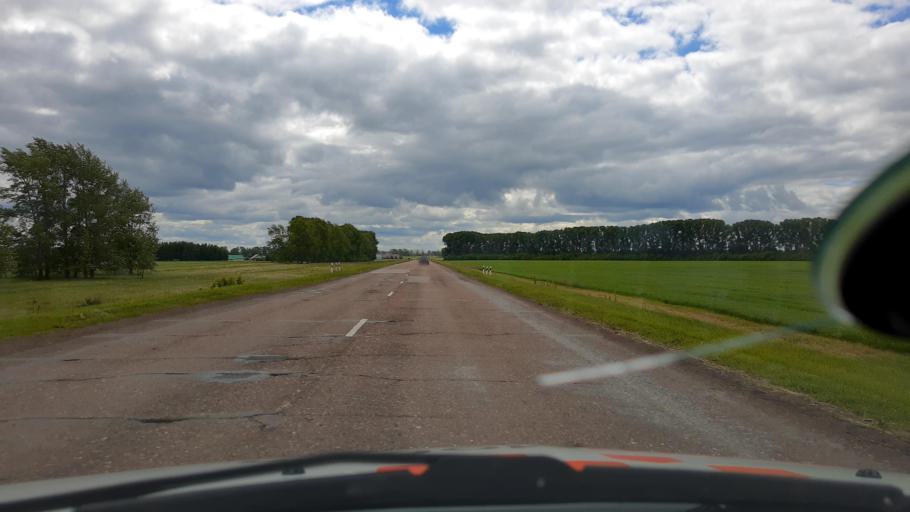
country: RU
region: Bashkortostan
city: Buzdyak
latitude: 54.7355
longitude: 54.5665
